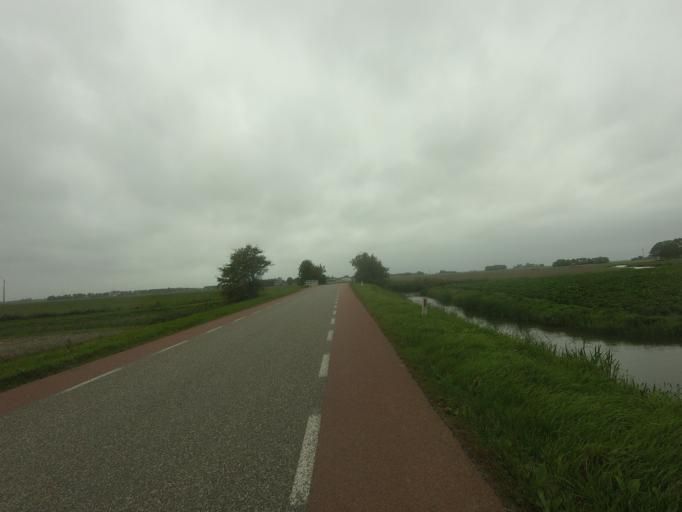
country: NL
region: Friesland
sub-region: Gemeente Ferwerderadiel
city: Ferwert
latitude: 53.3346
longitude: 5.8476
